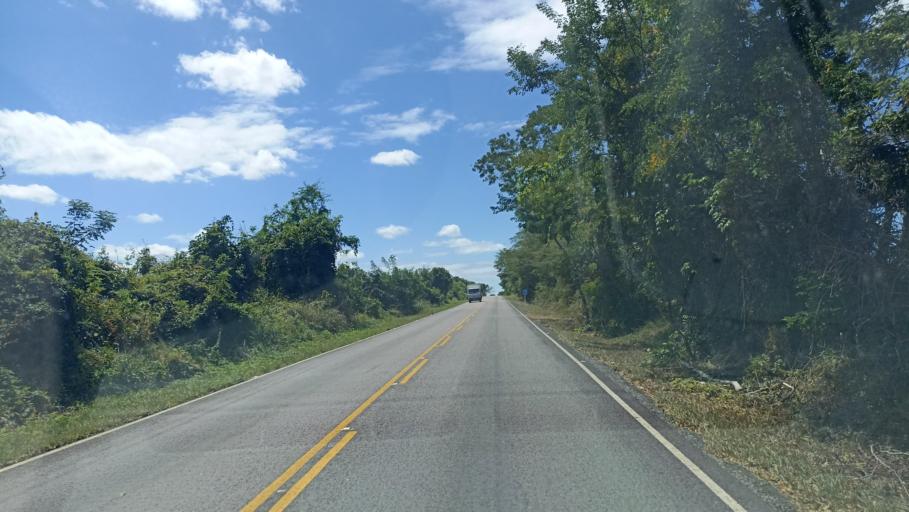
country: BR
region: Bahia
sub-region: Andarai
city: Vera Cruz
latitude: -12.7500
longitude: -41.3268
